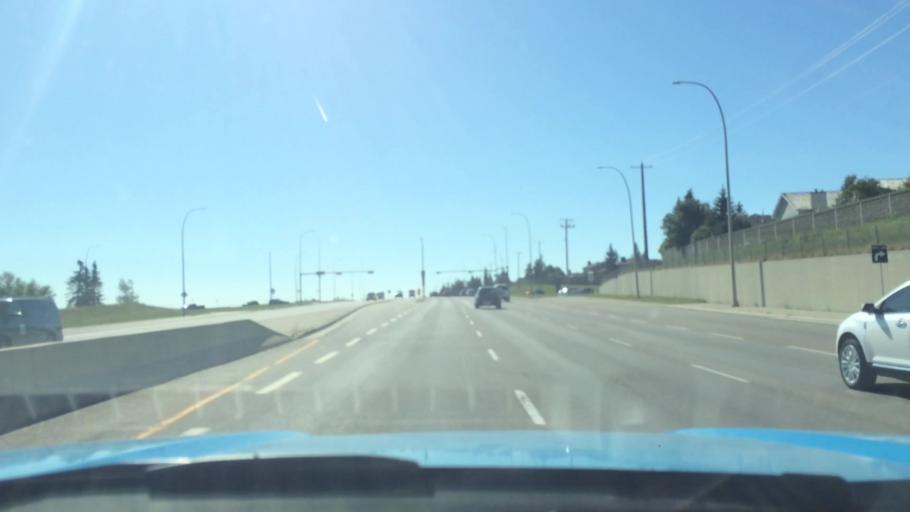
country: CA
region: Alberta
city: Calgary
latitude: 51.1391
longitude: -114.0840
